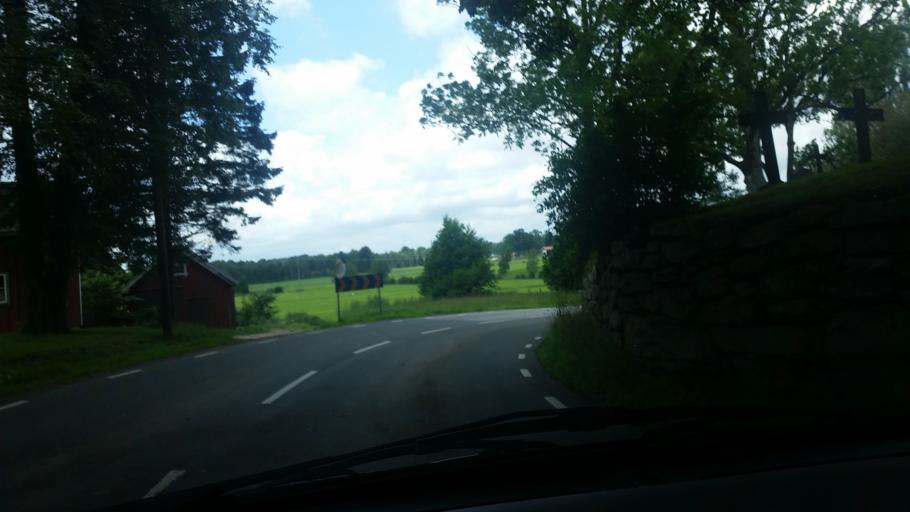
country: SE
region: Joenkoeping
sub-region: Gislaveds Kommun
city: Reftele
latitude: 57.1812
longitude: 13.5659
